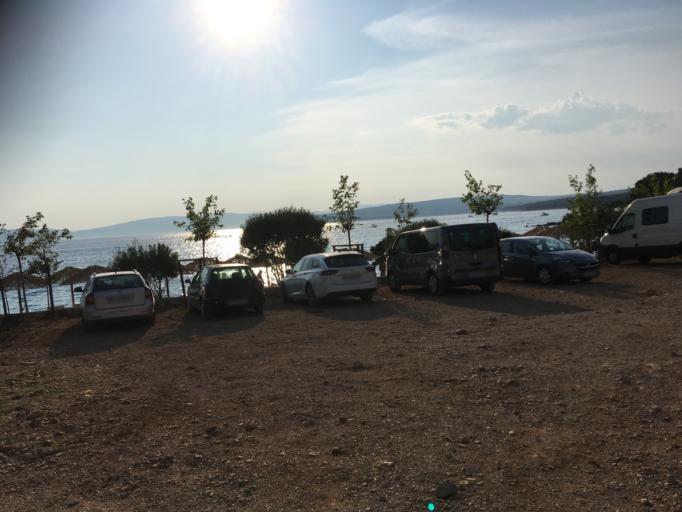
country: HR
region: Primorsko-Goranska
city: Punat
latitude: 45.0067
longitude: 14.6250
